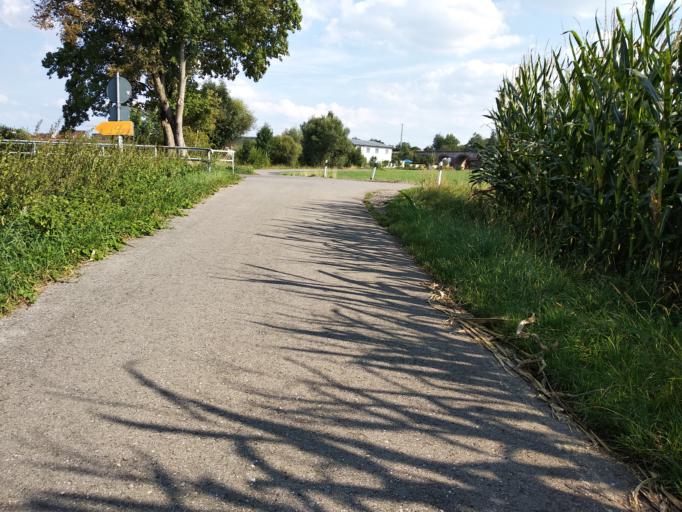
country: DE
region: Bavaria
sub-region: Swabia
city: Westerheim
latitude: 48.0183
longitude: 10.2969
